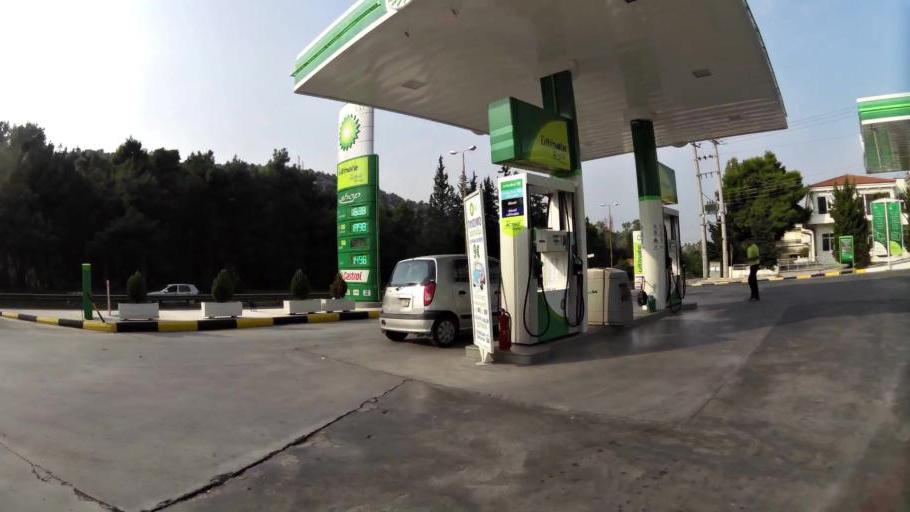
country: GR
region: Attica
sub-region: Nomarchia Athinas
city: Chaidari
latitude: 38.0139
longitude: 23.6346
